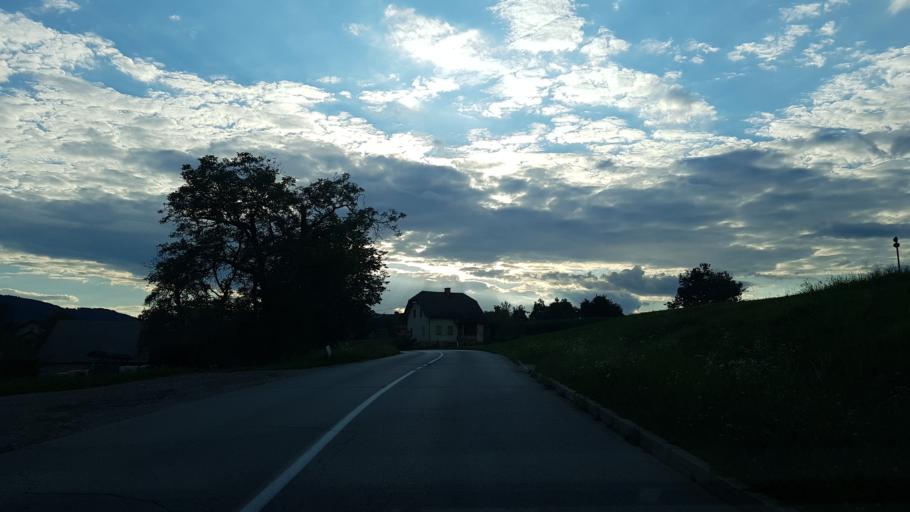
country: SI
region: Naklo
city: Naklo
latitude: 46.2582
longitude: 14.3069
